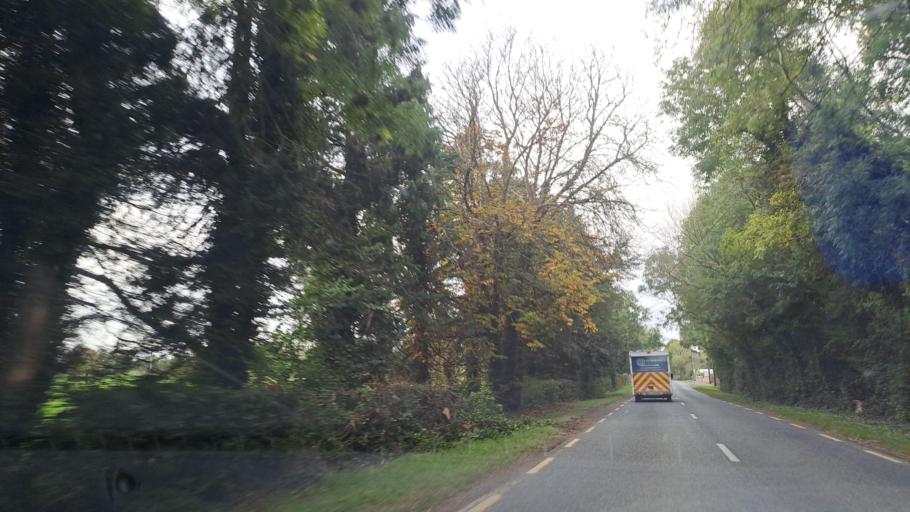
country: IE
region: Leinster
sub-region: An Mhi
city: Navan
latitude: 53.7440
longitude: -6.7166
